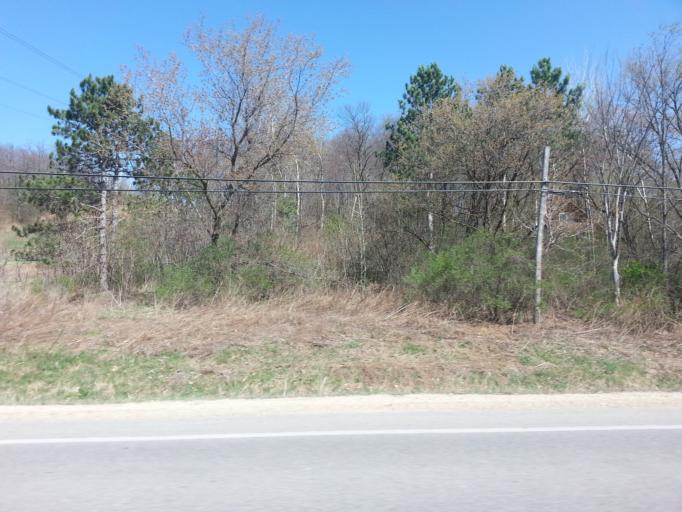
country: US
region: Wisconsin
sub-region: Dunn County
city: Menomonie
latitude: 44.8330
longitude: -91.9267
